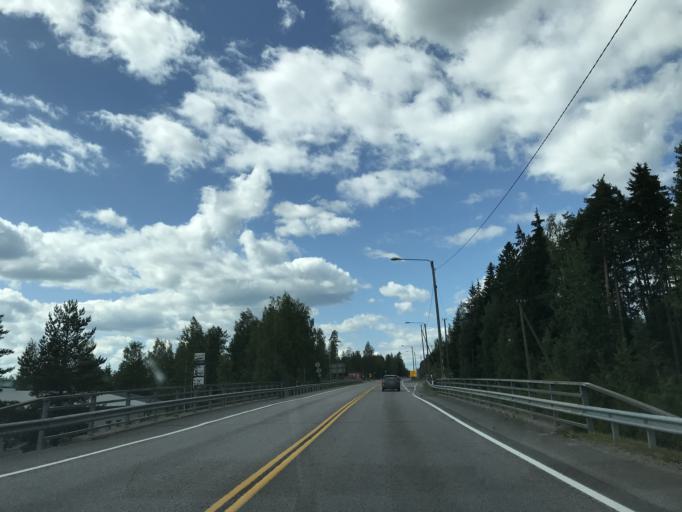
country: FI
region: Uusimaa
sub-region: Helsinki
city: Maentsaelae
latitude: 60.6257
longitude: 25.2916
